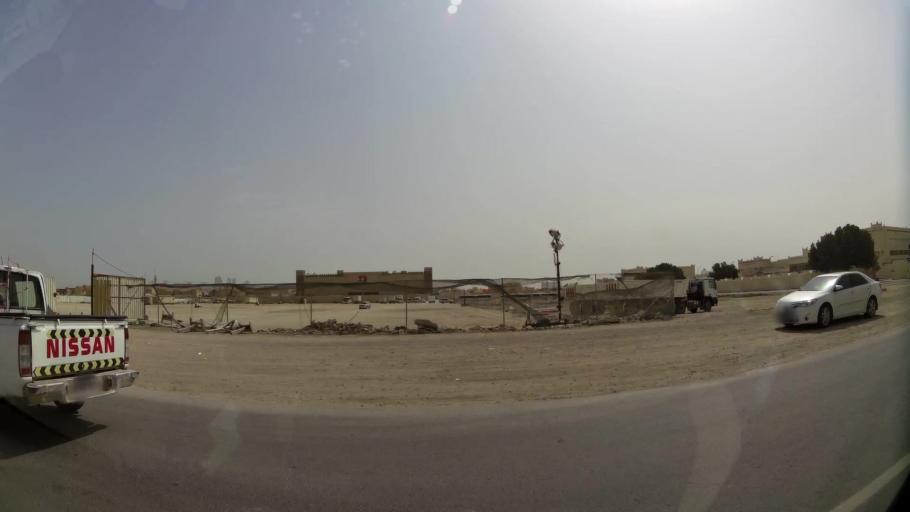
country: QA
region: Baladiyat ad Dawhah
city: Doha
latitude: 25.3008
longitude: 51.4850
